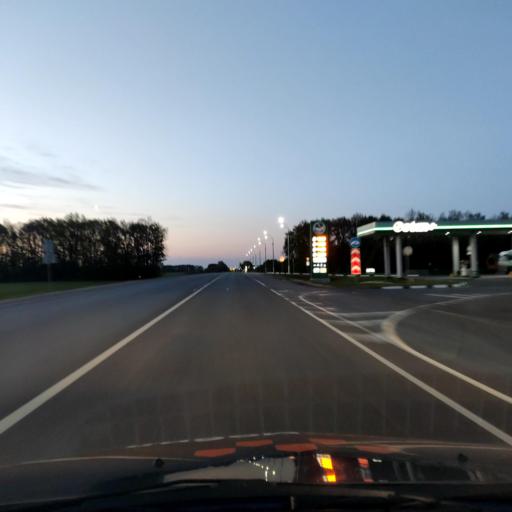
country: RU
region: Orjol
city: Zmiyevka
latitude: 52.7147
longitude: 36.3448
